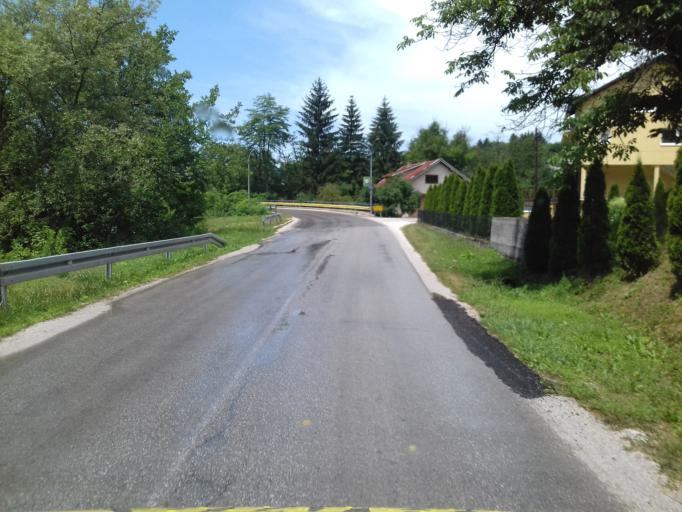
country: BA
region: Federation of Bosnia and Herzegovina
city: Kiseljak
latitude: 43.9505
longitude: 18.0887
